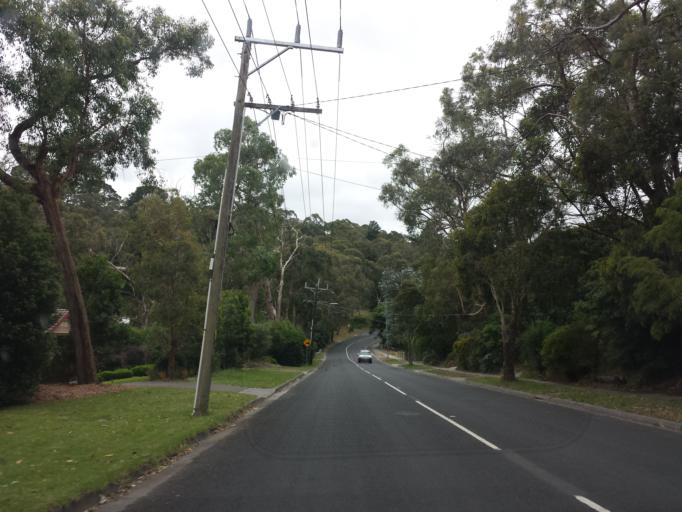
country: AU
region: Victoria
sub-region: Yarra Ranges
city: Tremont
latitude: -37.9164
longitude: 145.3238
